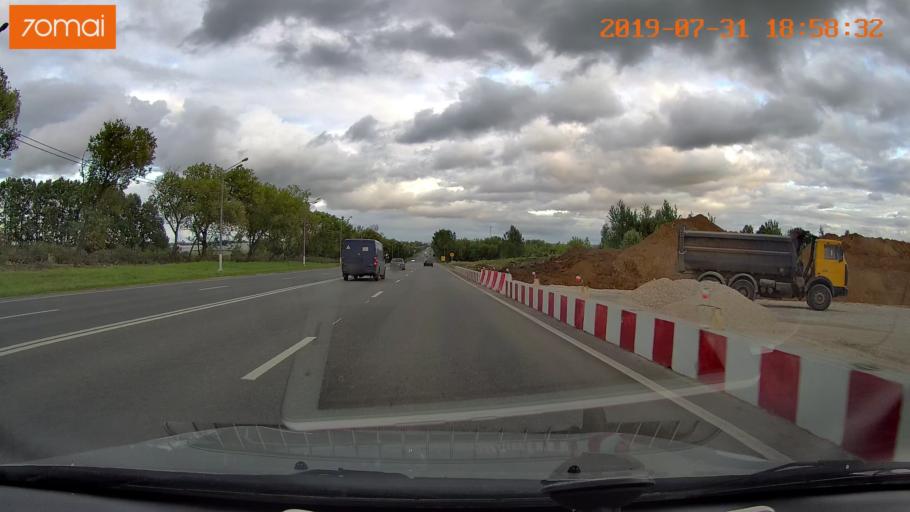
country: RU
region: Moskovskaya
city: Raduzhnyy
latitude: 55.1461
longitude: 38.7055
